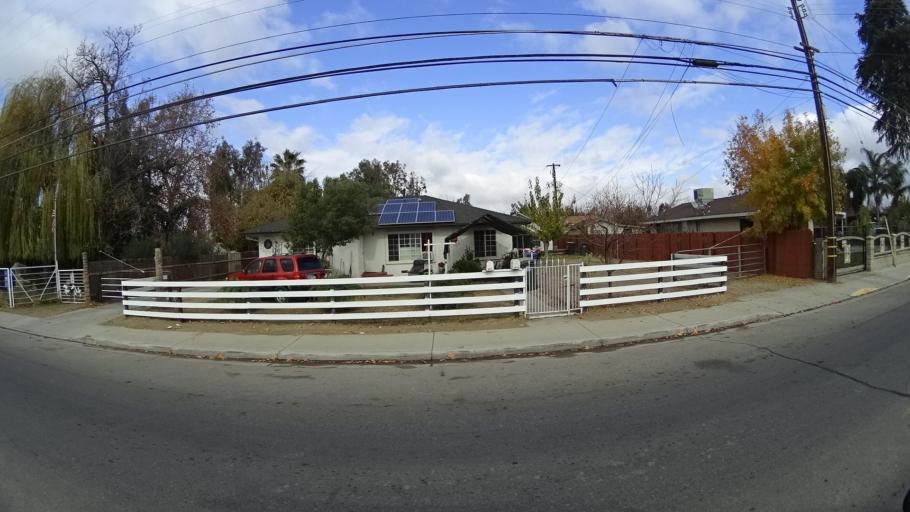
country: US
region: California
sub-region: Kern County
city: Bakersfield
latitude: 35.3395
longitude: -118.9960
